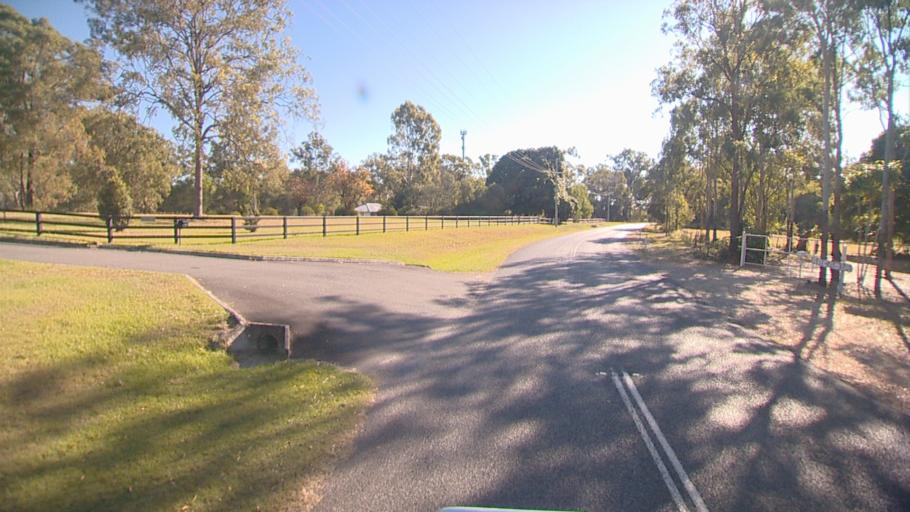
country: AU
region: Queensland
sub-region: Logan
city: Chambers Flat
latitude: -27.7485
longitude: 153.0863
